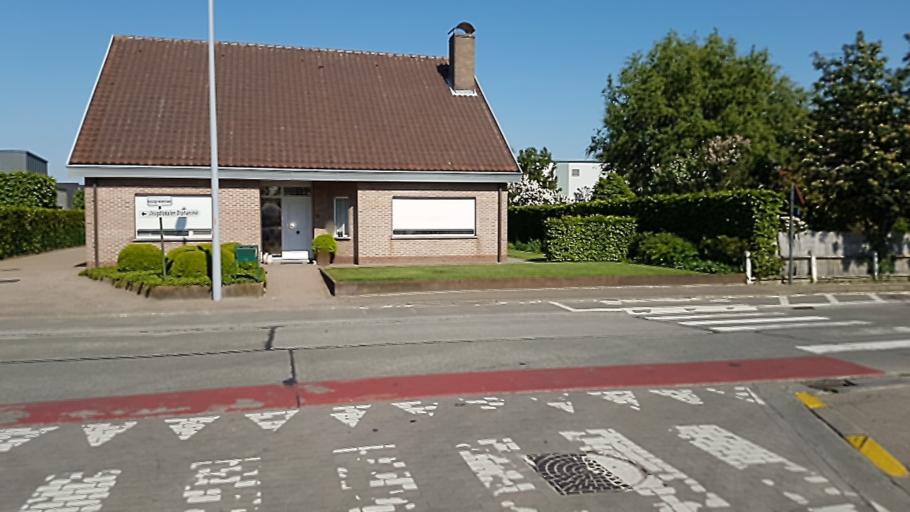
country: BE
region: Flanders
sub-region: Provincie Oost-Vlaanderen
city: Lochristi
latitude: 51.0975
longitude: 3.8309
